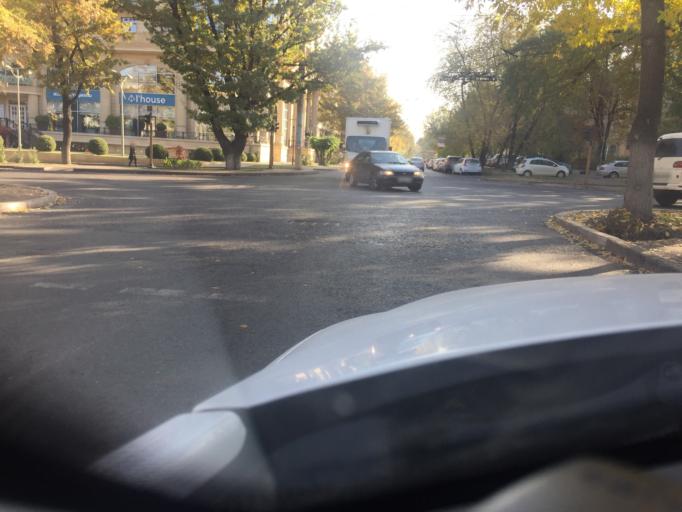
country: KZ
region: Almaty Qalasy
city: Almaty
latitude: 43.2450
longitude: 76.9029
